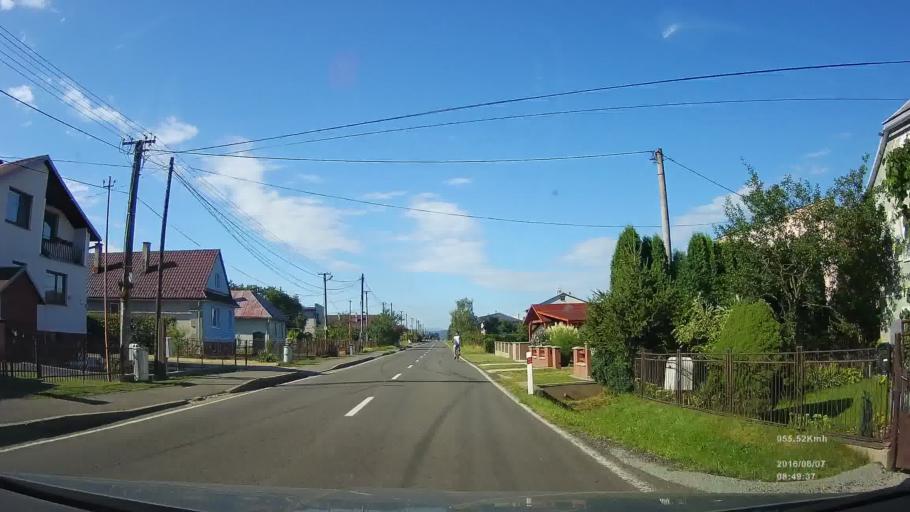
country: SK
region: Presovsky
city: Stropkov
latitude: 49.2516
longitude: 21.6875
